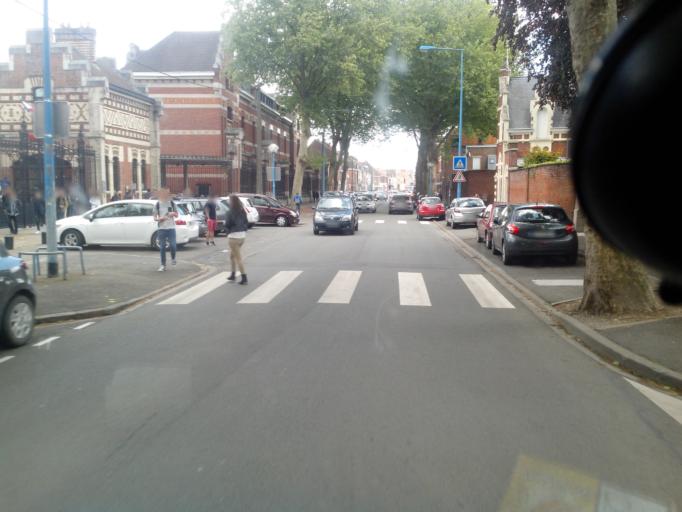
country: FR
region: Nord-Pas-de-Calais
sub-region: Departement du Nord
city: Armentieres
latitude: 50.6877
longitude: 2.8726
